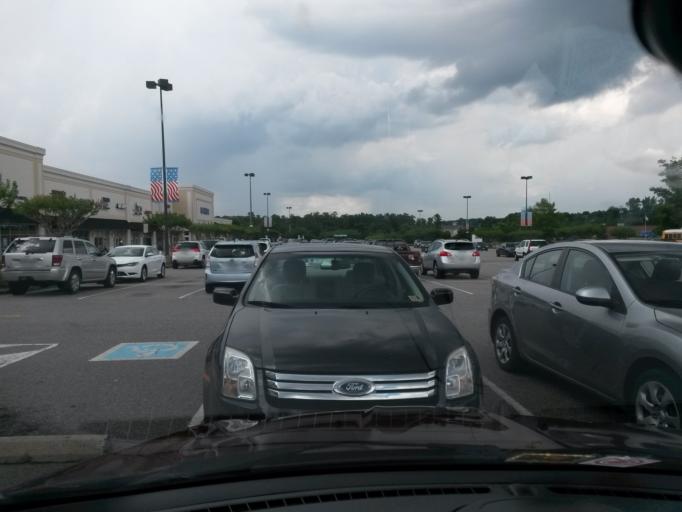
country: US
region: Virginia
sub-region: Chesterfield County
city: Chester
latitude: 37.3593
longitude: -77.4170
